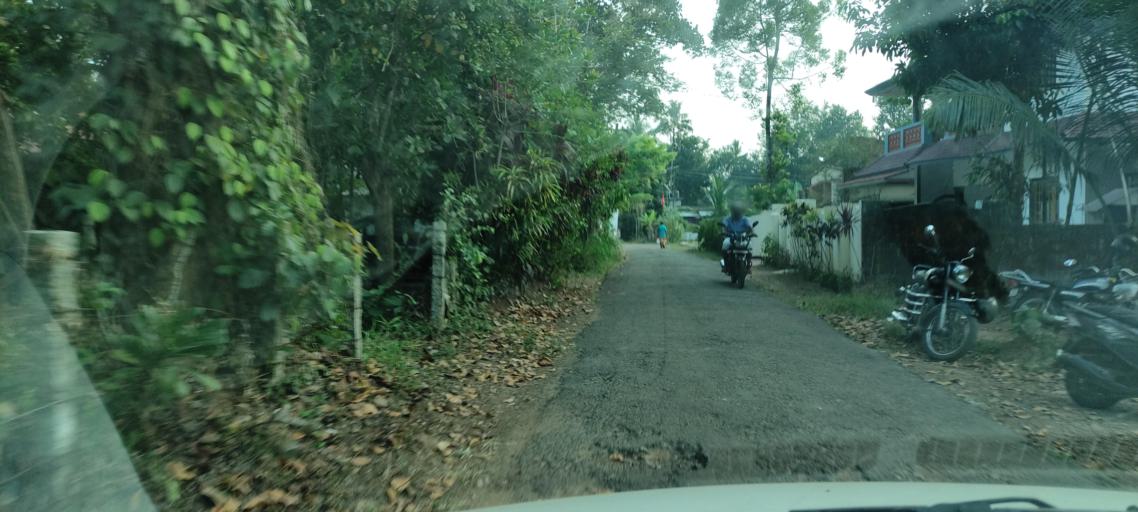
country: IN
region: Kerala
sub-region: Alappuzha
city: Kattanam
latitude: 9.1682
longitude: 76.5911
